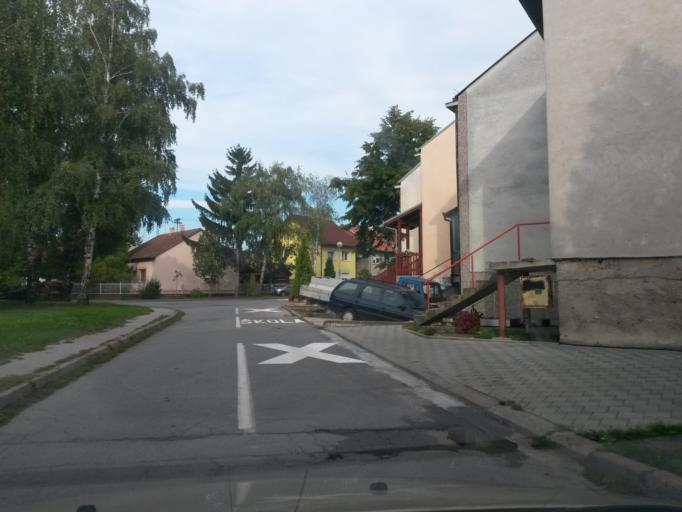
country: HR
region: Osjecko-Baranjska
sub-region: Grad Osijek
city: Osijek
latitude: 45.5587
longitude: 18.7288
